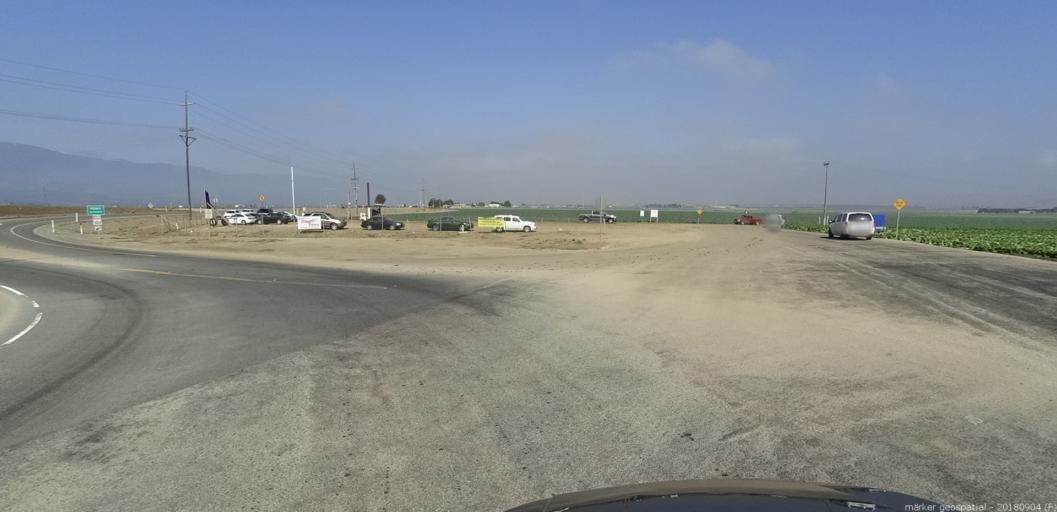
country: US
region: California
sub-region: Monterey County
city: Soledad
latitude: 36.4344
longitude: -121.3373
